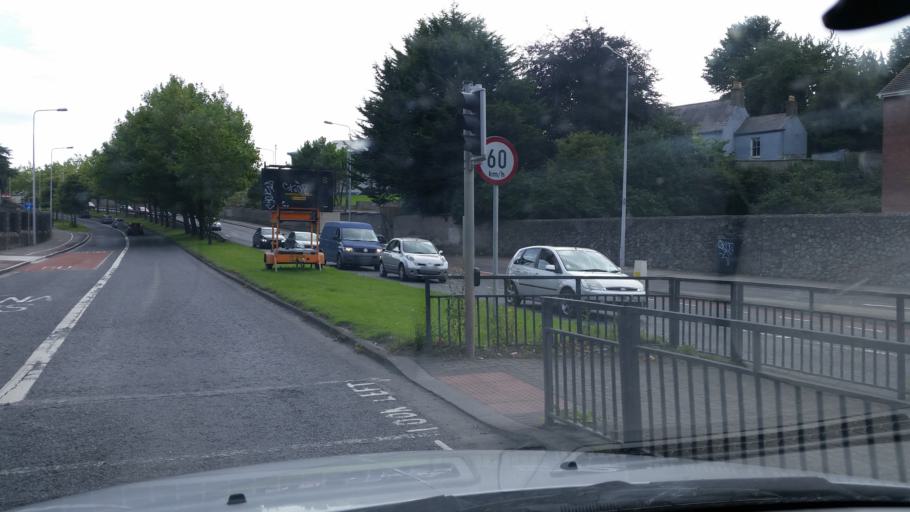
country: IE
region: Leinster
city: Cabra
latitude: 53.3758
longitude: -6.2863
